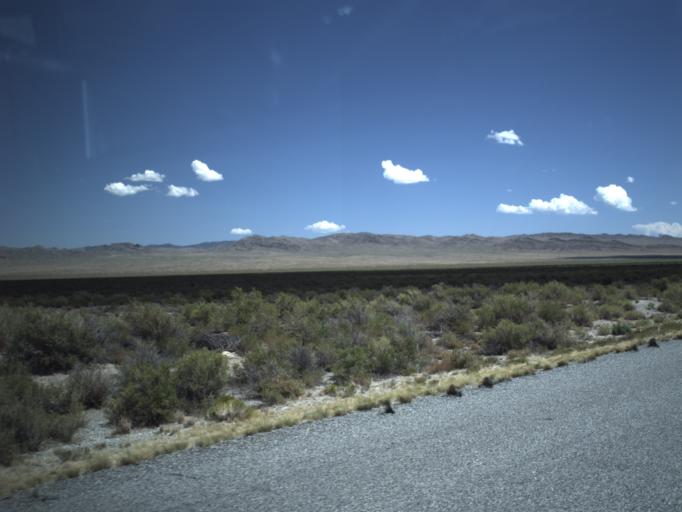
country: US
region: Nevada
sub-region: White Pine County
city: McGill
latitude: 39.0498
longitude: -113.9535
